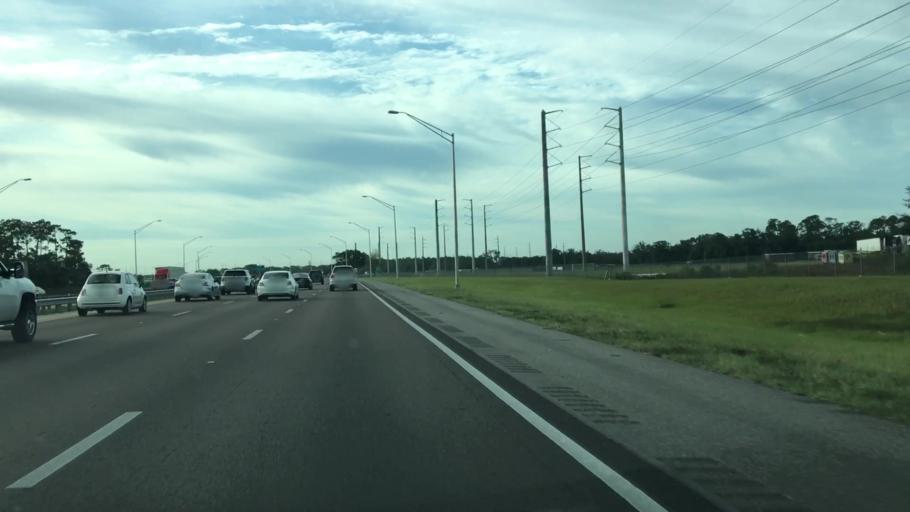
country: US
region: Florida
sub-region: Orange County
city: Azalea Park
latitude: 28.5200
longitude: -81.2509
